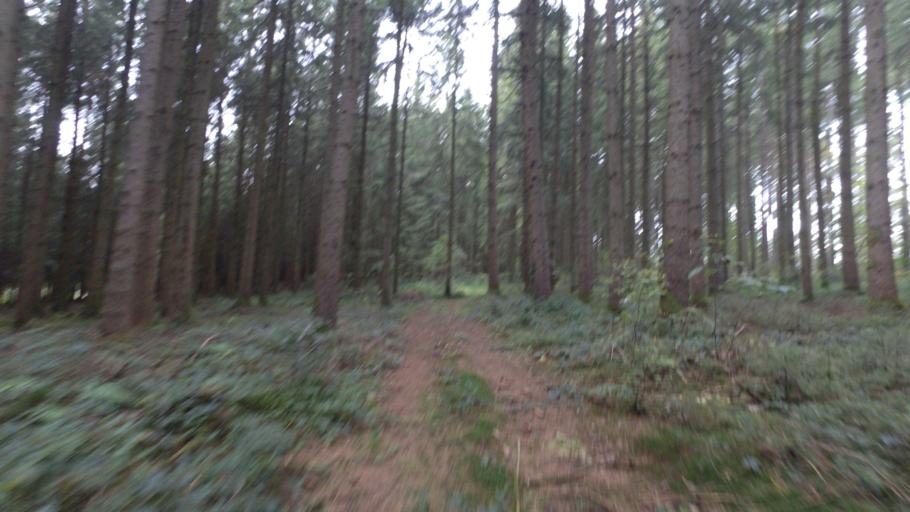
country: DE
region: Bavaria
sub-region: Upper Bavaria
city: Chieming
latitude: 47.9165
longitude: 12.5507
